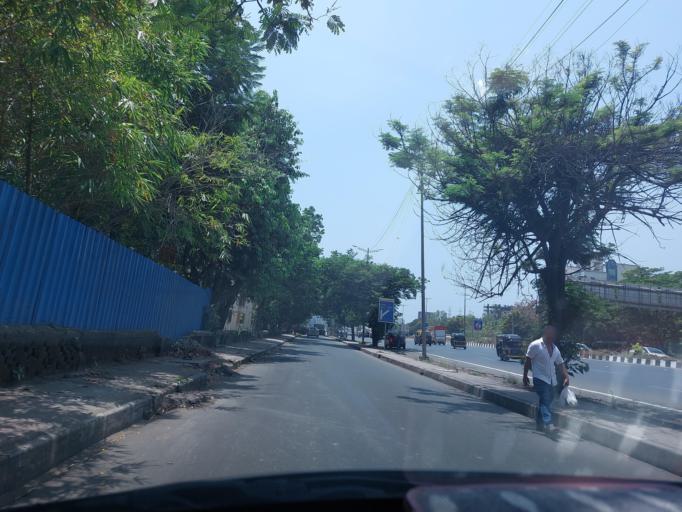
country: IN
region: Maharashtra
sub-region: Mumbai Suburban
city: Mumbai
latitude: 19.0509
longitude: 72.8760
